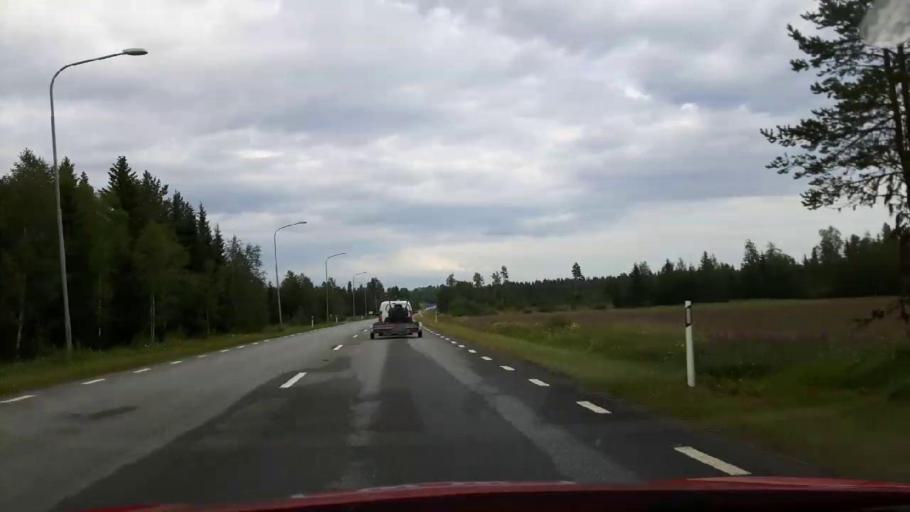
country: SE
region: Jaemtland
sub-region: Stroemsunds Kommun
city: Stroemsund
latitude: 63.6736
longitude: 15.3937
